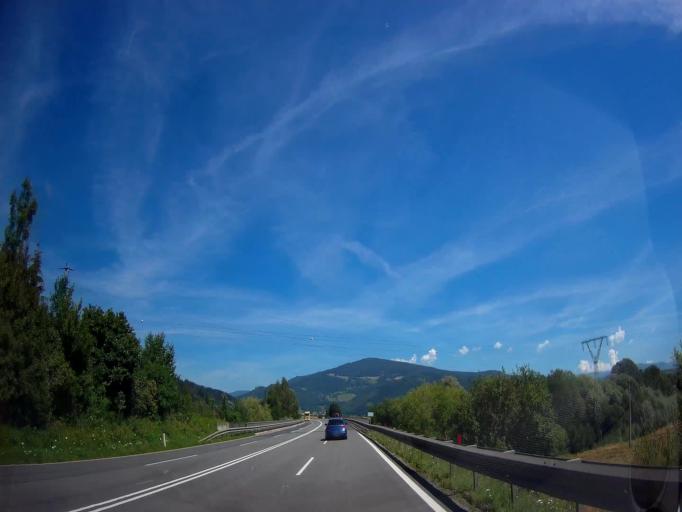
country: AT
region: Carinthia
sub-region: Politischer Bezirk Sankt Veit an der Glan
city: Molbling
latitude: 46.8585
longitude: 14.4493
